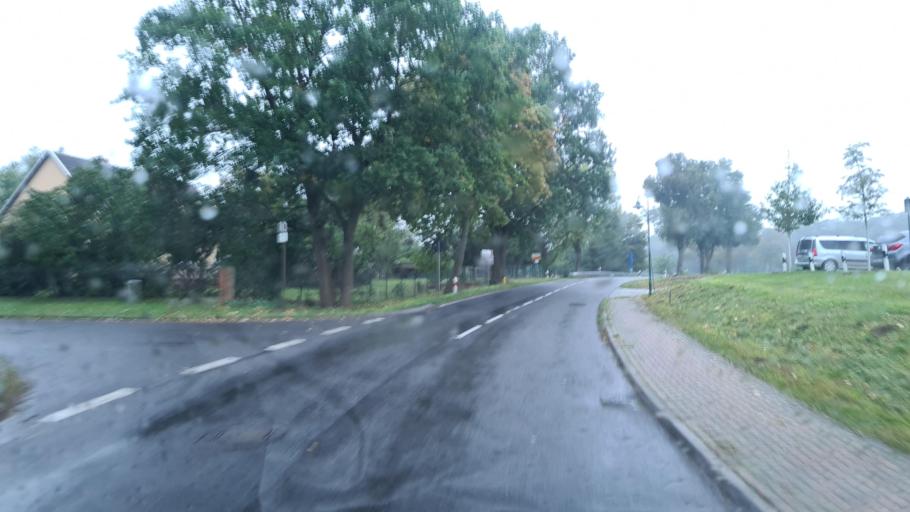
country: DE
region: Brandenburg
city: Rietz Neuendorf
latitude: 52.2130
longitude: 14.1994
